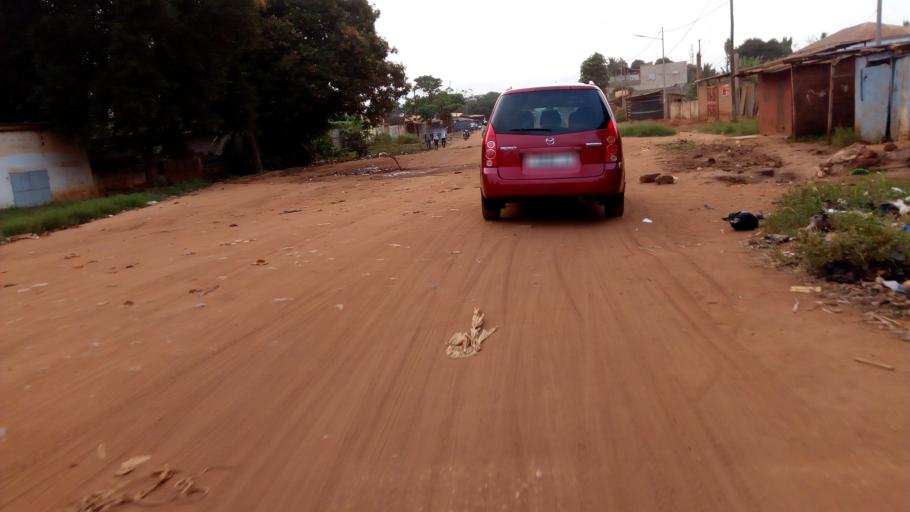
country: TG
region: Maritime
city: Lome
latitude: 6.2311
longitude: 1.1942
